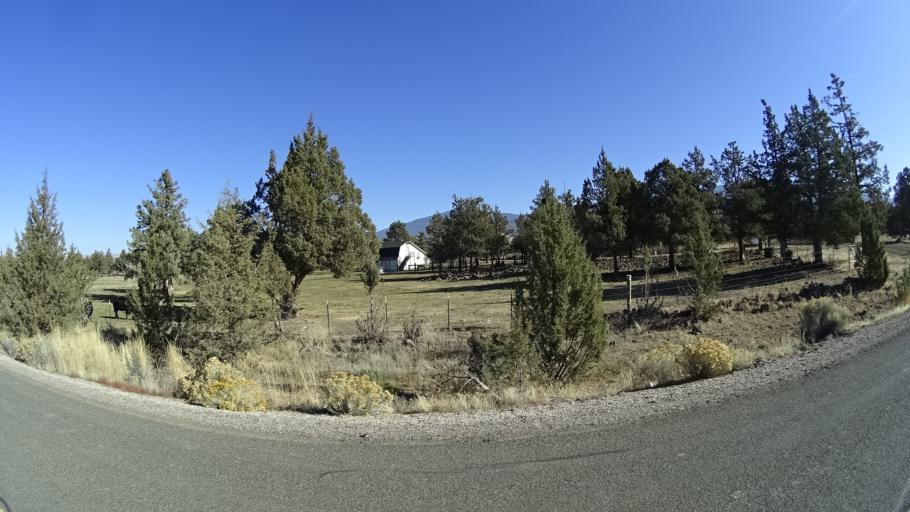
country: US
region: California
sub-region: Siskiyou County
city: Montague
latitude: 41.6534
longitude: -122.3616
